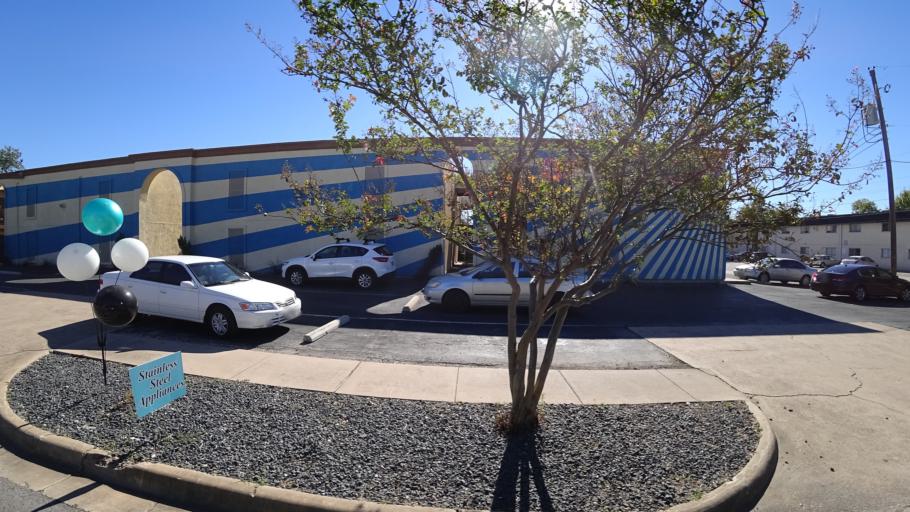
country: US
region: Texas
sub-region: Travis County
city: Austin
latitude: 30.3246
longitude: -97.7369
